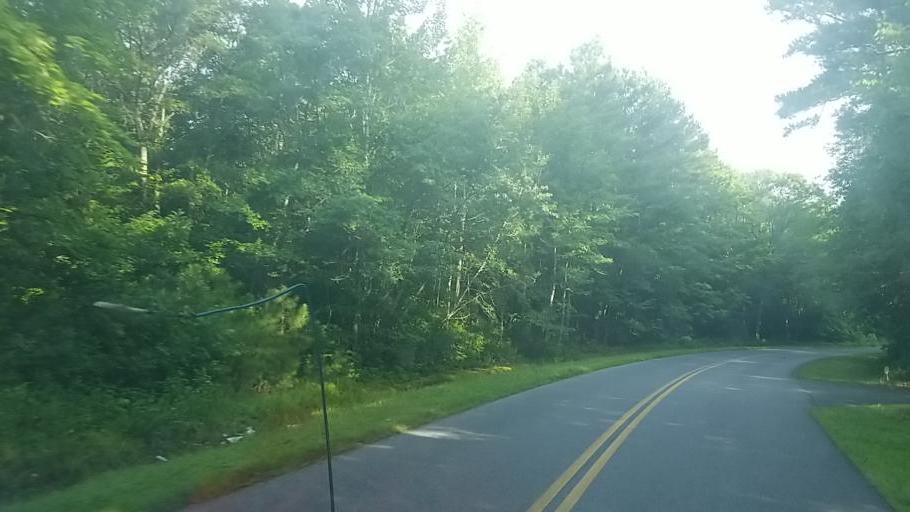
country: US
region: Maryland
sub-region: Worcester County
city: West Ocean City
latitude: 38.3193
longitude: -75.1467
